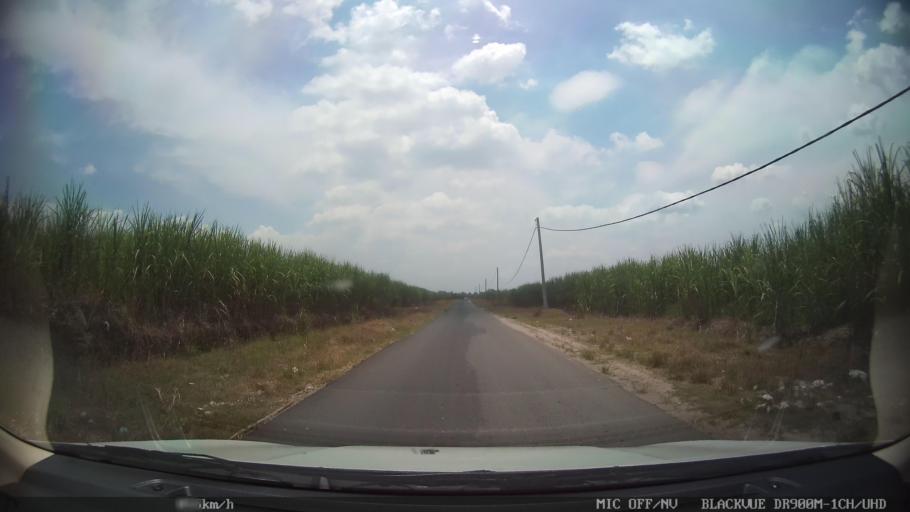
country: ID
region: North Sumatra
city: Binjai
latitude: 3.5927
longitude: 98.5379
